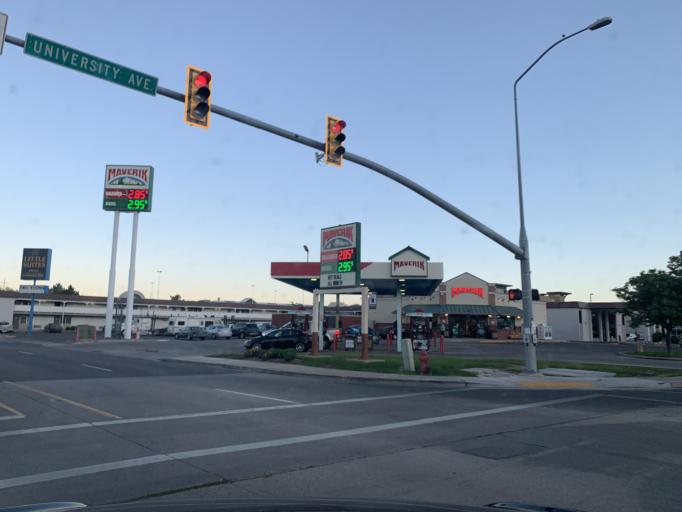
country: US
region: Utah
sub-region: Utah County
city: Provo
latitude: 40.2147
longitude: -111.6591
